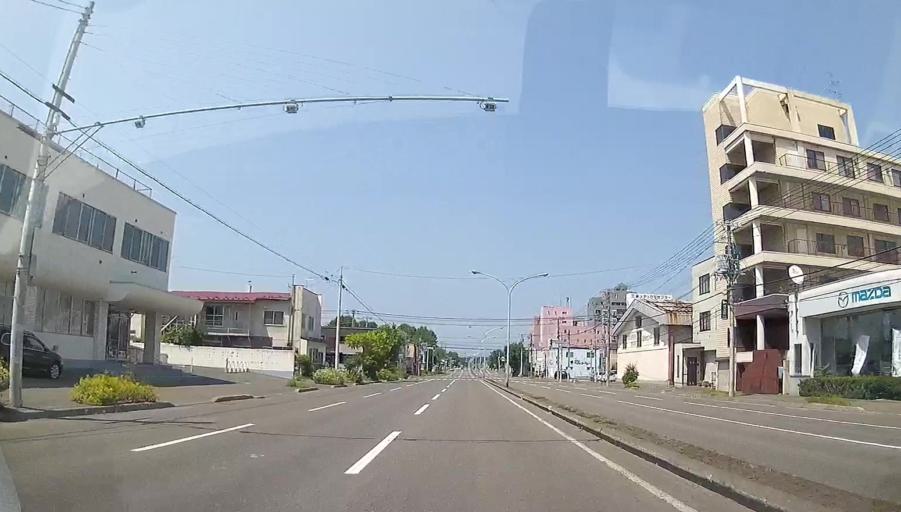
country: JP
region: Hokkaido
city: Obihiro
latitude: 42.9261
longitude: 143.1999
